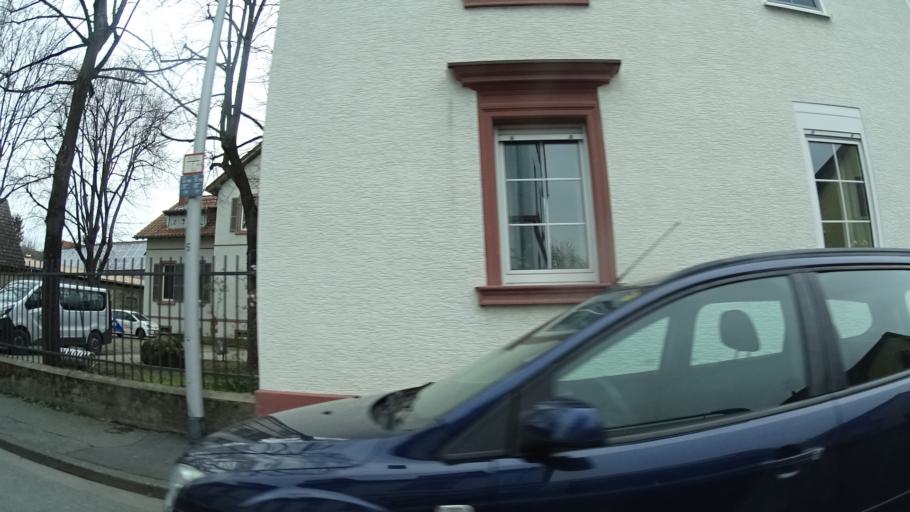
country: DE
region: Hesse
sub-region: Regierungsbezirk Darmstadt
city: Stockstadt am Rhein
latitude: 49.8360
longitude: 8.4674
